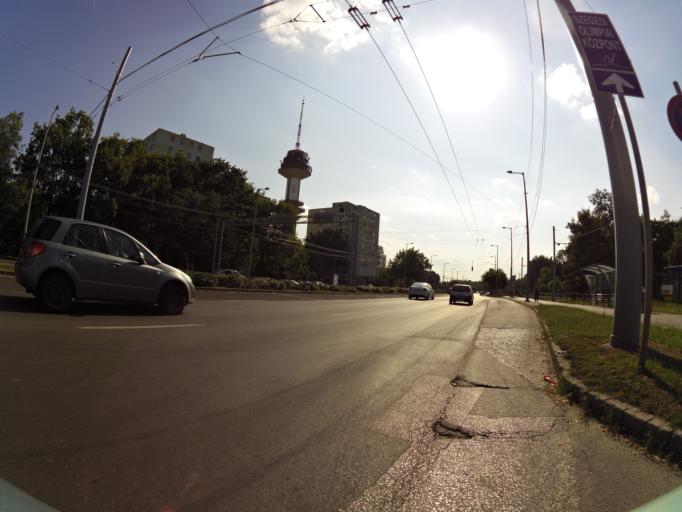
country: HU
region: Csongrad
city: Szeged
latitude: 46.2724
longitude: 20.1479
